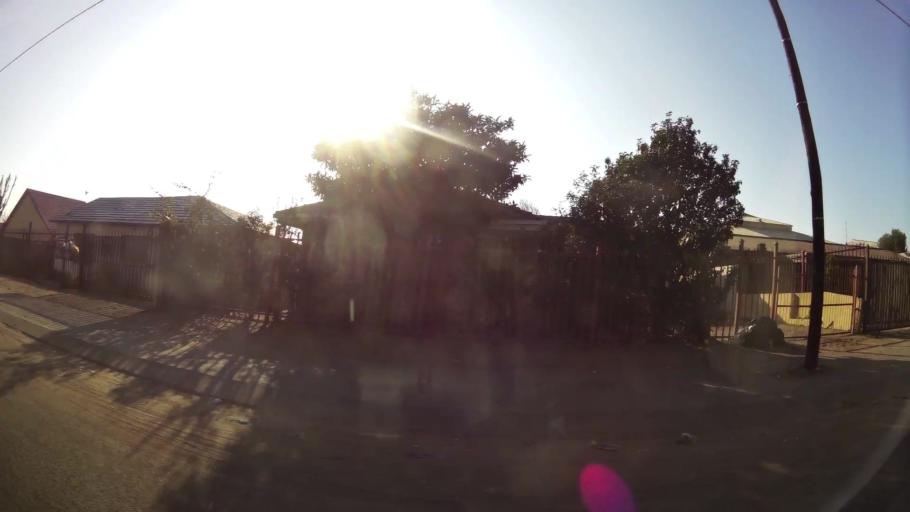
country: ZA
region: Orange Free State
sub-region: Mangaung Metropolitan Municipality
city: Bloemfontein
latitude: -29.1433
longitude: 26.2483
